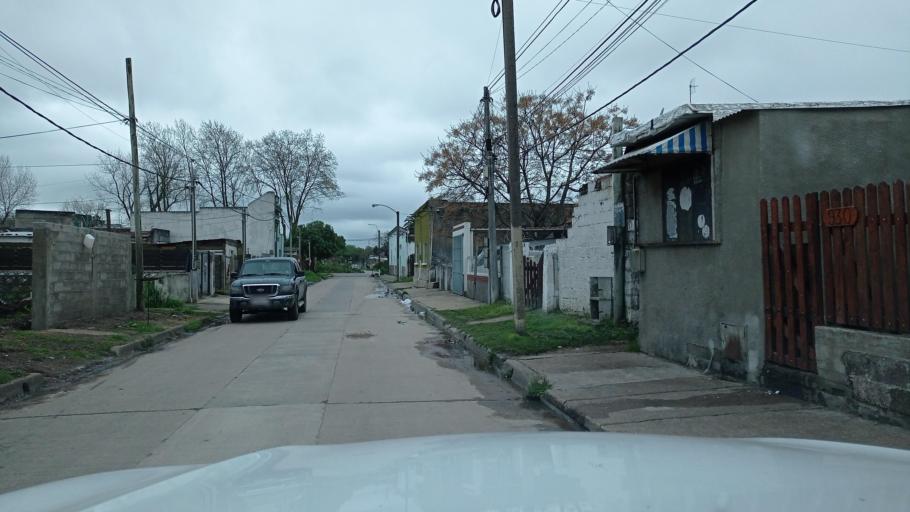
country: UY
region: Canelones
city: La Paz
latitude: -34.8392
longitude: -56.2358
